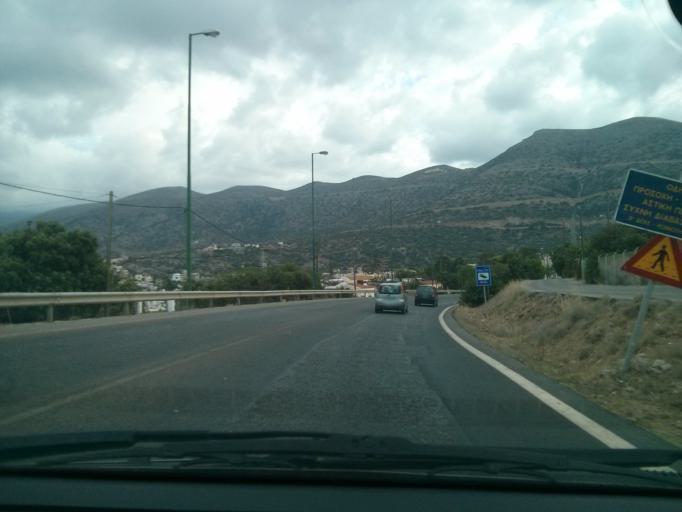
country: GR
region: Crete
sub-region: Nomos Irakleiou
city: Stalis
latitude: 35.2995
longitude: 25.4218
